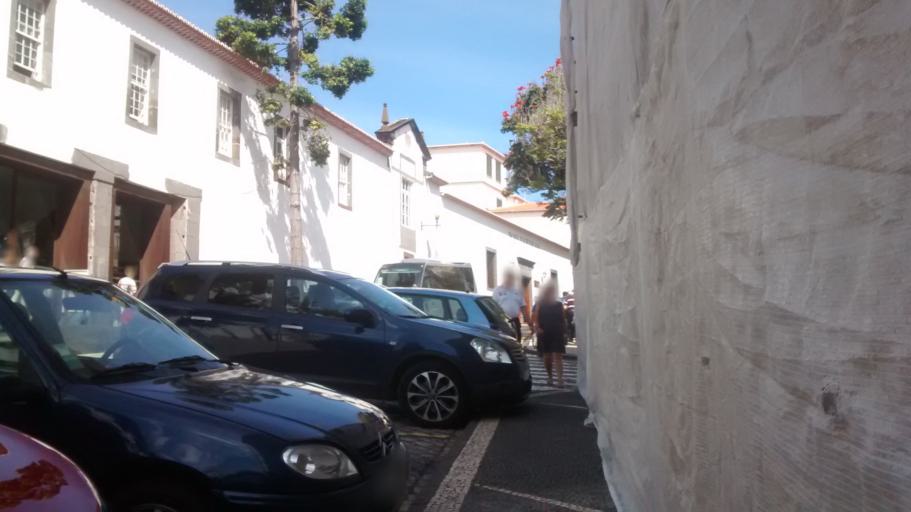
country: PT
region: Madeira
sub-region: Funchal
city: Nossa Senhora do Monte
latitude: 32.6501
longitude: -16.9090
